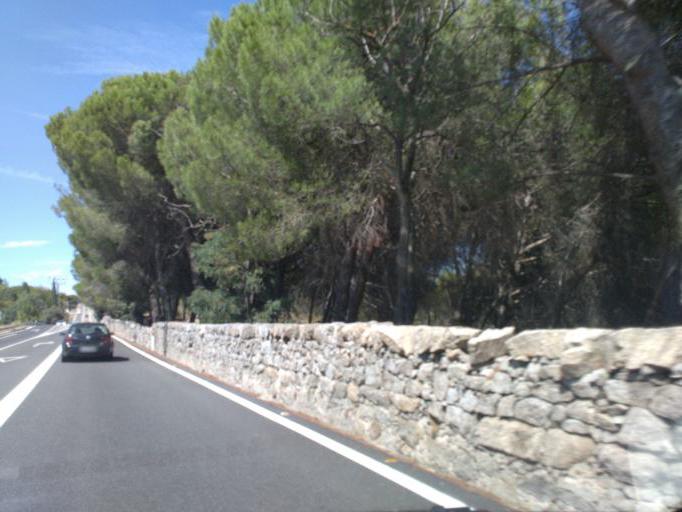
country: ES
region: Madrid
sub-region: Provincia de Madrid
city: Torrelodones
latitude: 40.5576
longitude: -3.9644
